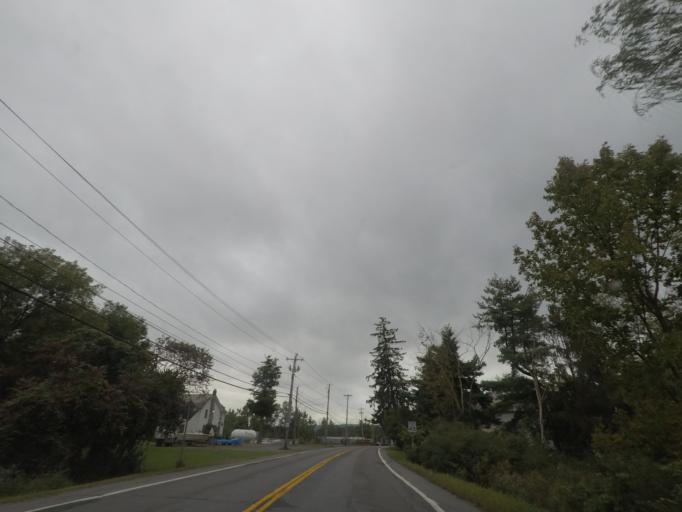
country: US
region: New York
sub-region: Rensselaer County
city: Hoosick Falls
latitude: 42.9184
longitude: -73.3500
